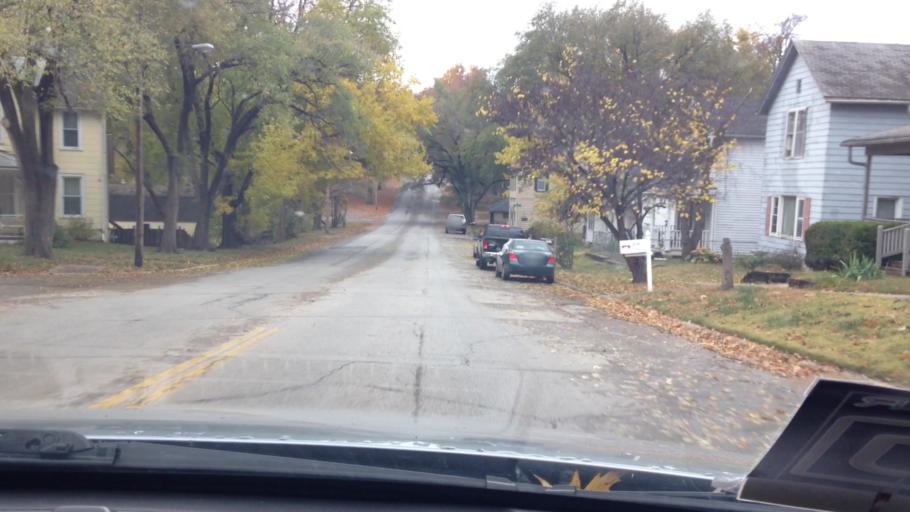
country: US
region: Kansas
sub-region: Leavenworth County
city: Leavenworth
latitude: 39.3072
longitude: -94.9136
